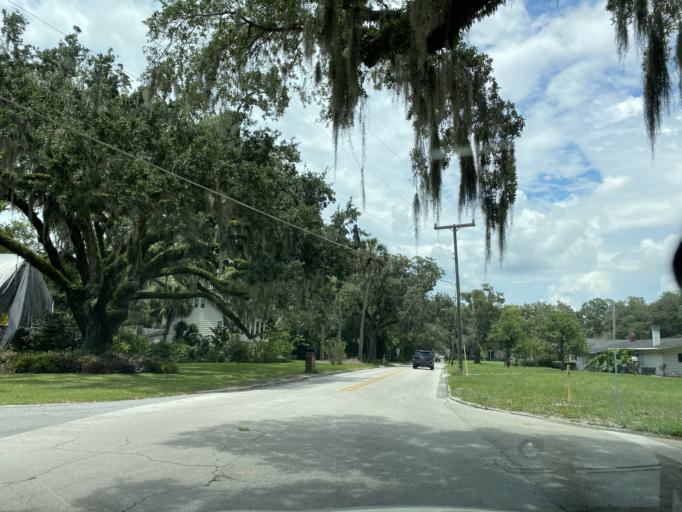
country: US
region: Florida
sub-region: Seminole County
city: Sanford
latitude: 28.7903
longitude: -81.2565
